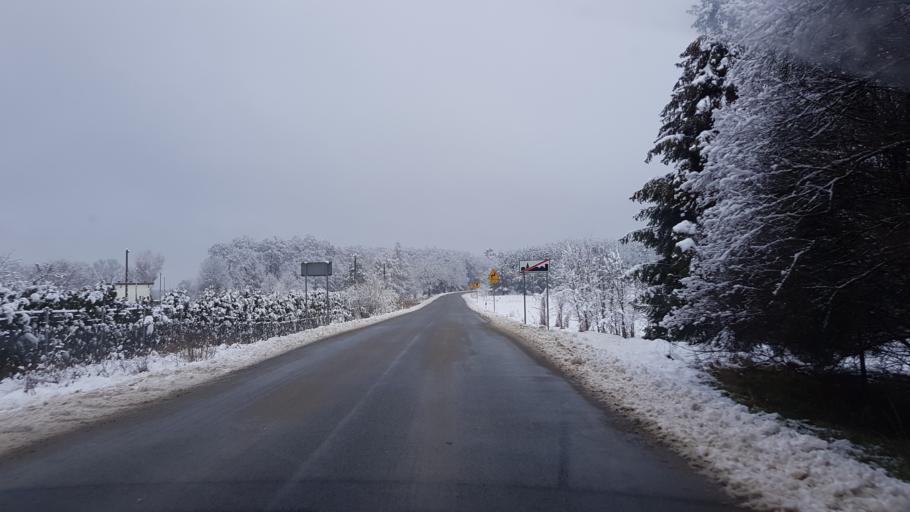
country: PL
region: West Pomeranian Voivodeship
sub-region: Powiat drawski
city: Zlocieniec
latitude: 53.6093
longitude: 16.0055
